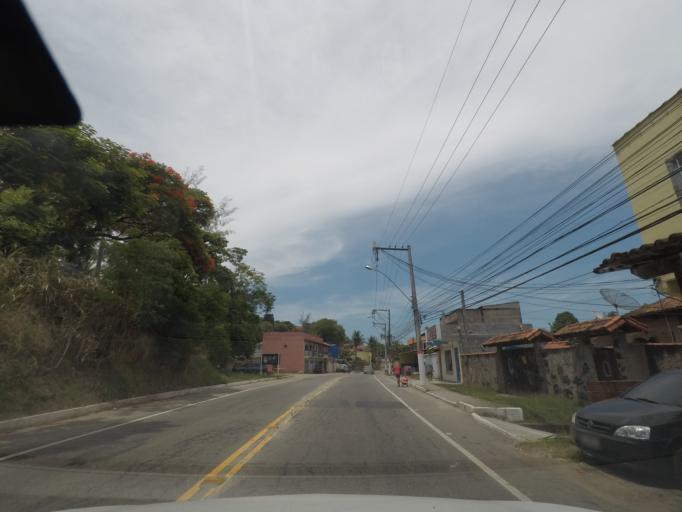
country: BR
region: Rio de Janeiro
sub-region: Marica
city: Marica
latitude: -22.9250
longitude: -42.8190
